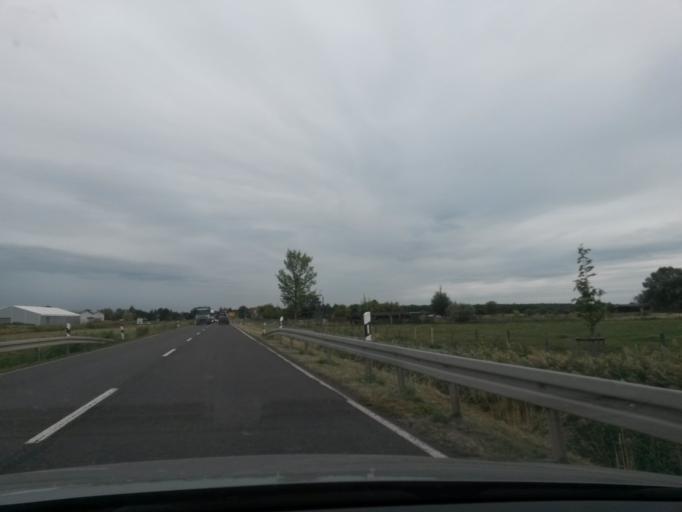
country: DE
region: Saxony-Anhalt
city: Schonhausen
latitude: 52.6054
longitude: 12.0375
